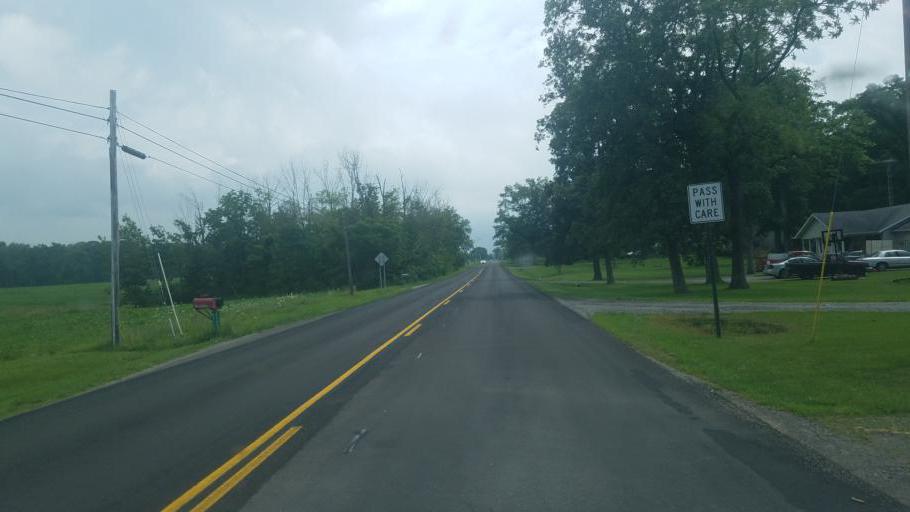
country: US
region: Ohio
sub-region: Logan County
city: Russells Point
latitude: 40.4701
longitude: -83.8406
